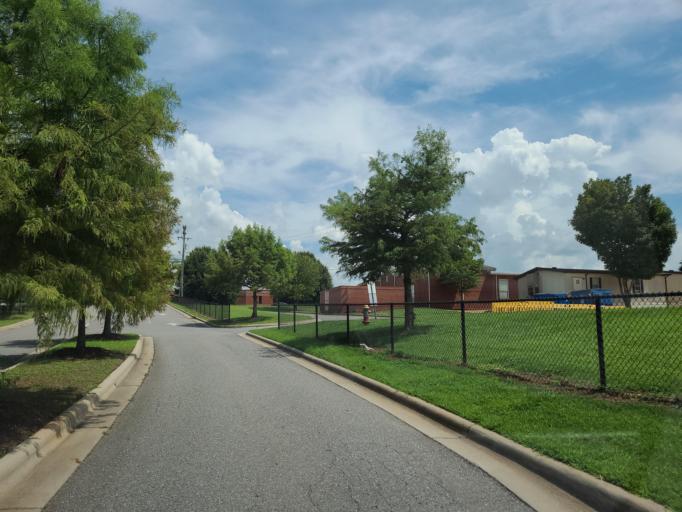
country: US
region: North Carolina
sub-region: Cleveland County
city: Shelby
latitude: 35.2808
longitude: -81.4944
